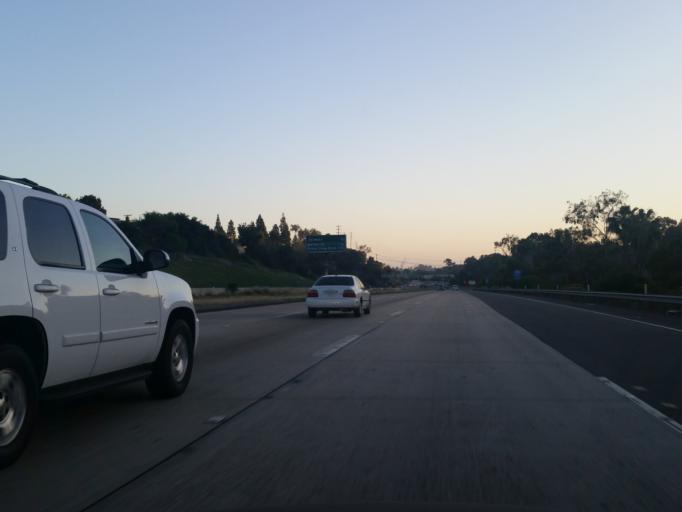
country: US
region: California
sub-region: San Diego County
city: San Diego
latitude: 32.7269
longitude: -117.1132
